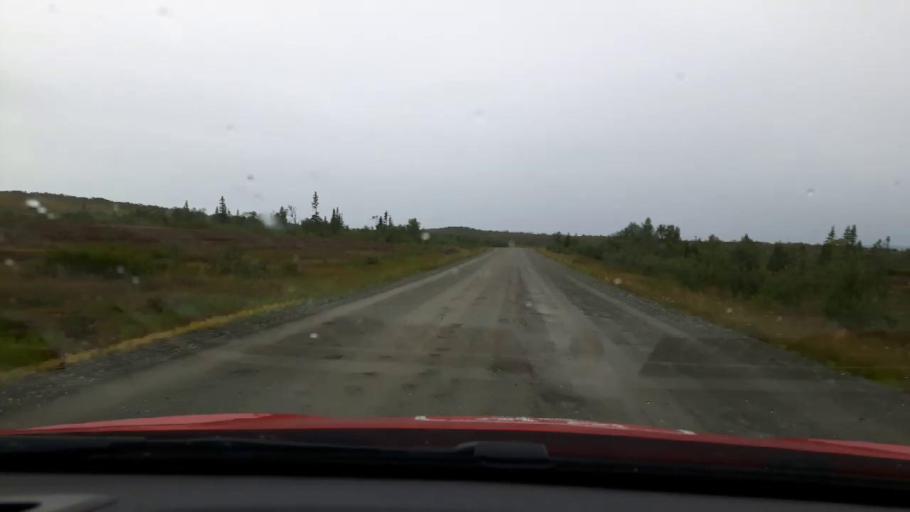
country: NO
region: Nord-Trondelag
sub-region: Meraker
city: Meraker
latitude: 63.6225
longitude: 12.2895
